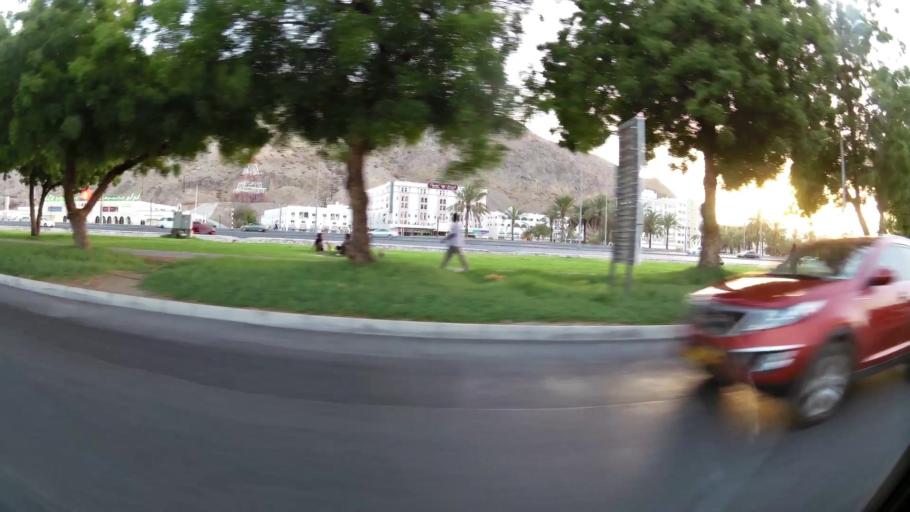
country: OM
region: Muhafazat Masqat
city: Muscat
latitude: 23.5810
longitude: 58.5629
